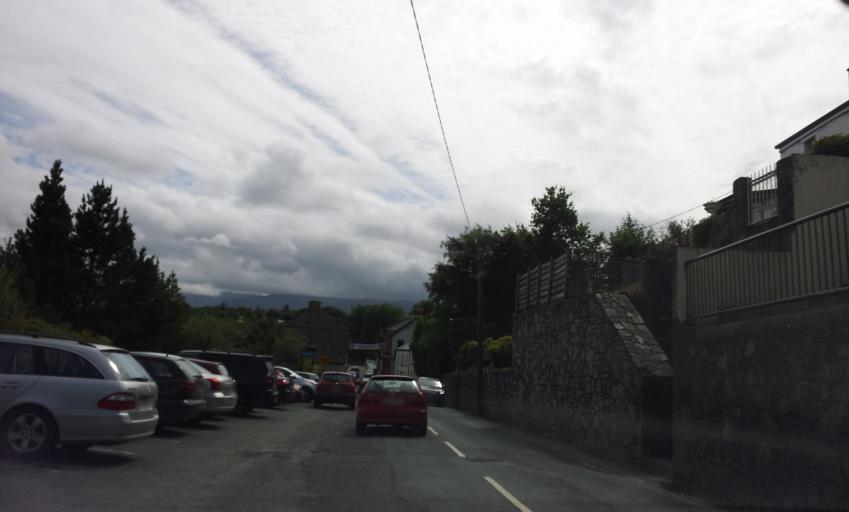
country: IE
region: Munster
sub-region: Ciarrai
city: Killorglin
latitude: 52.1076
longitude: -9.7852
